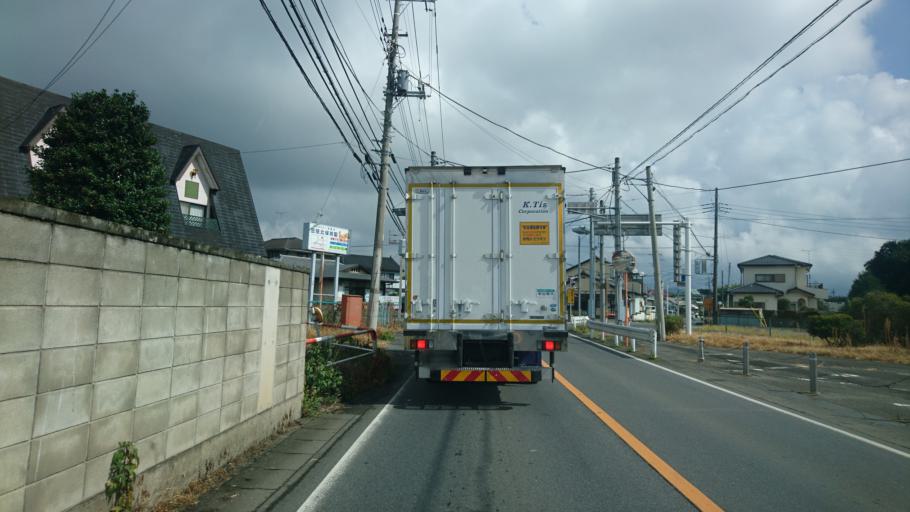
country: JP
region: Gunma
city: Omamacho-omama
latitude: 36.4000
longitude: 139.2830
